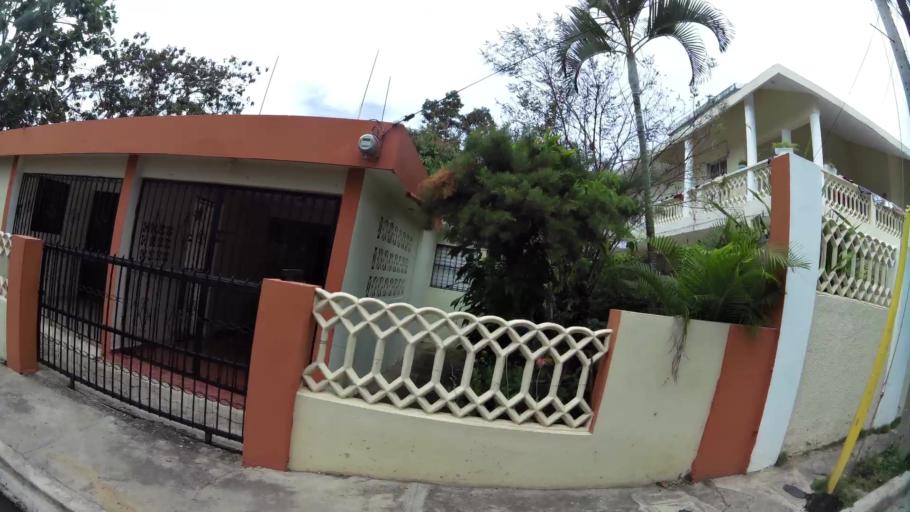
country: DO
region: Santiago
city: Santiago de los Caballeros
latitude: 19.4269
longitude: -70.6682
